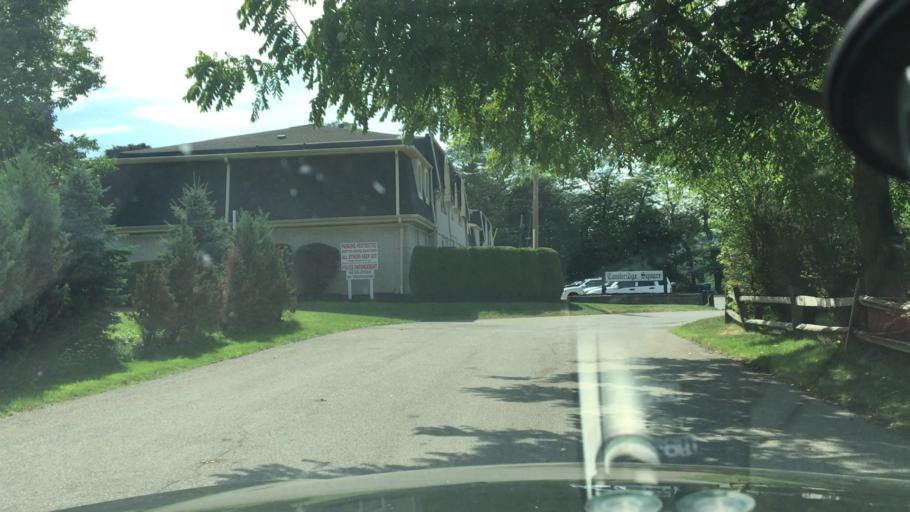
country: US
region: New York
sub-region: Erie County
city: Harris Hill
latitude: 42.9786
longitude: -78.7026
